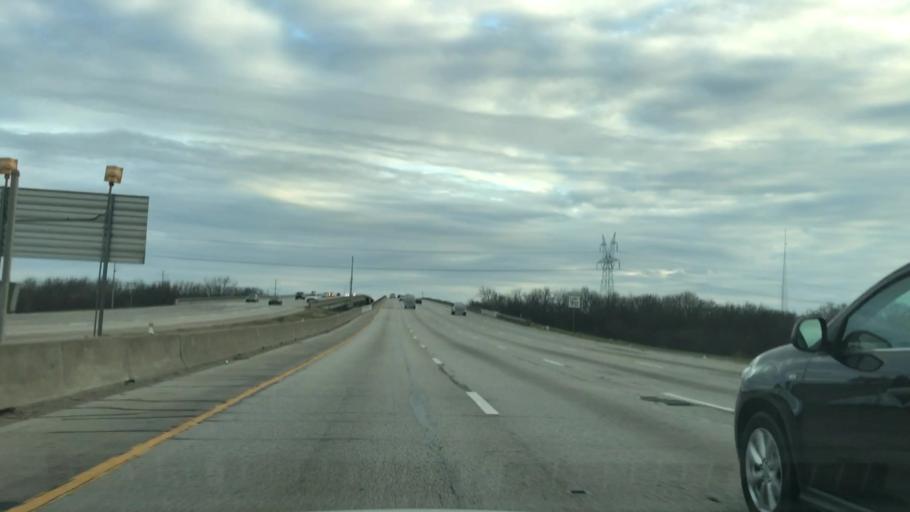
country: US
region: Texas
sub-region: Dallas County
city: Irving
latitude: 32.7906
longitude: -96.9199
